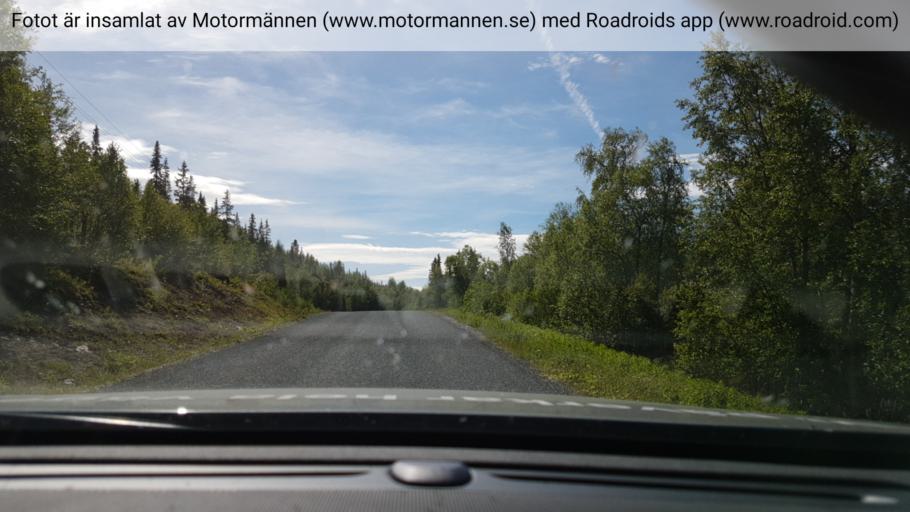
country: SE
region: Vaesterbotten
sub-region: Vilhelmina Kommun
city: Sjoberg
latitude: 65.3080
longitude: 15.2944
